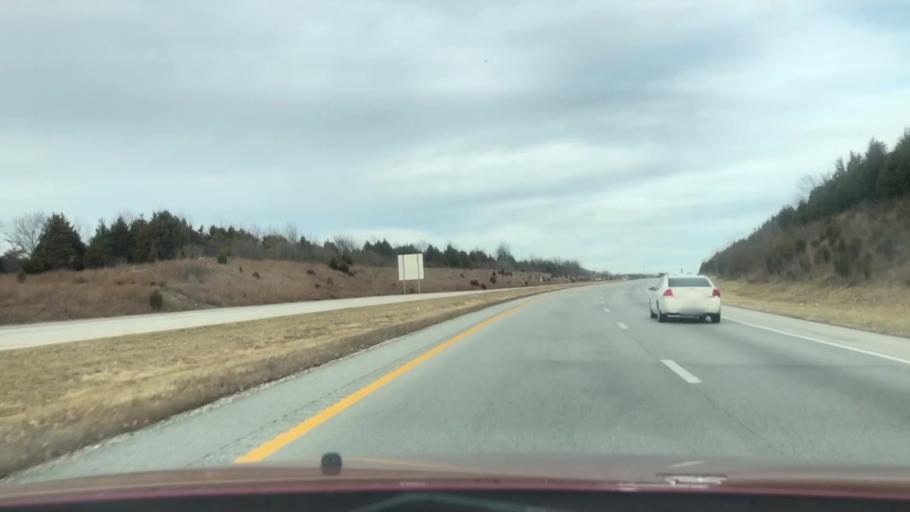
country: US
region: Missouri
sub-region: Greene County
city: Springfield
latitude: 37.2668
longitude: -93.2227
